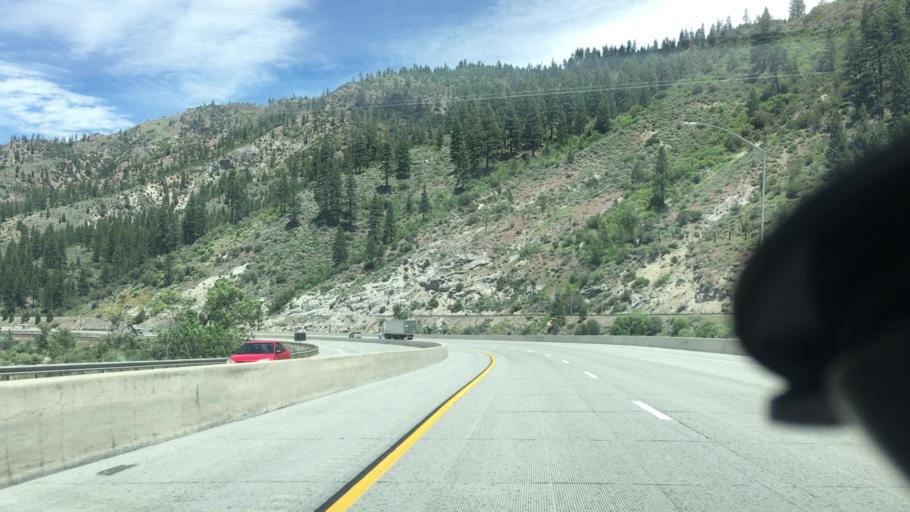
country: US
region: Nevada
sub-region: Washoe County
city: Verdi
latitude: 39.3968
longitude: -120.0232
